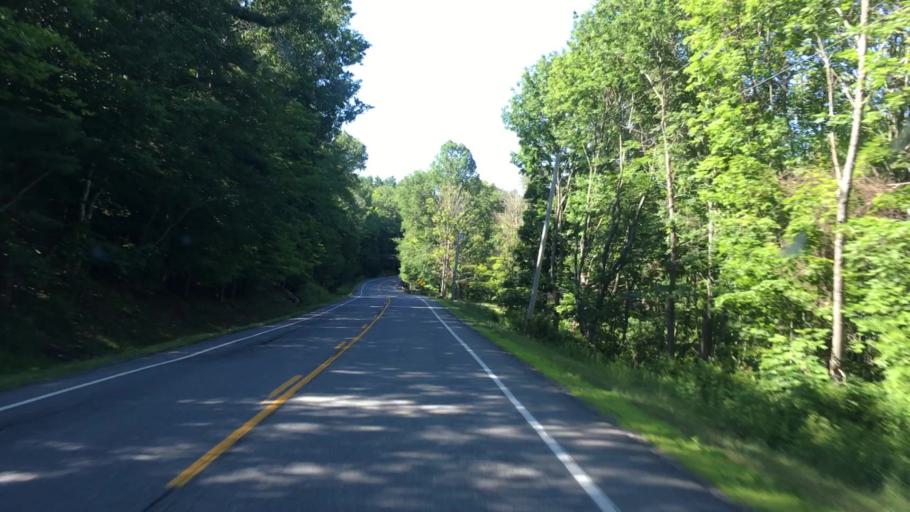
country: US
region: Maine
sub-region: Hancock County
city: Dedham
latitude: 44.6654
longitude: -68.6748
